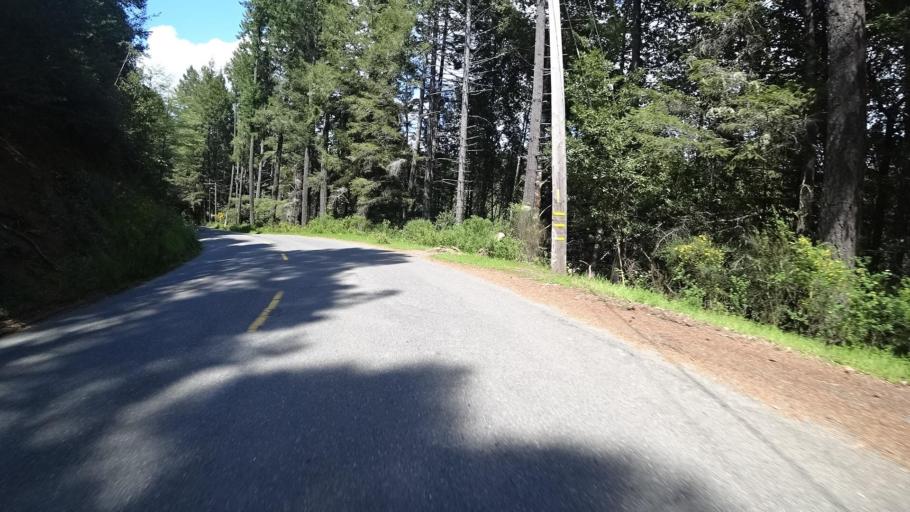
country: US
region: California
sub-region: Humboldt County
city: Redway
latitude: 40.0902
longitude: -123.9373
